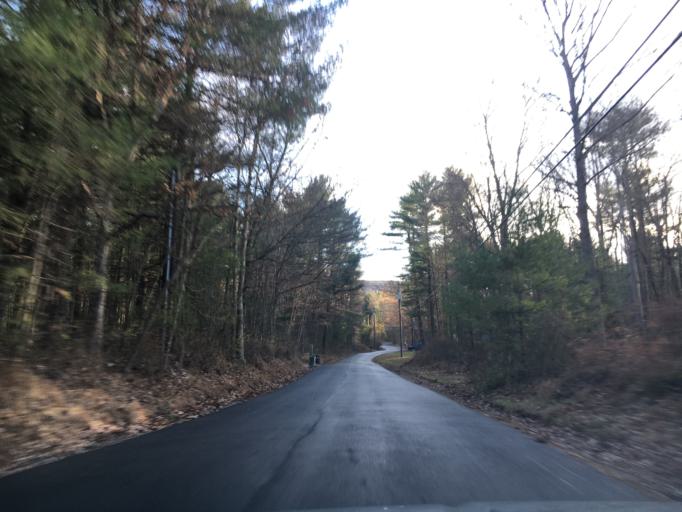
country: US
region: Pennsylvania
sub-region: Carbon County
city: Lehighton
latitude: 40.7755
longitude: -75.7106
